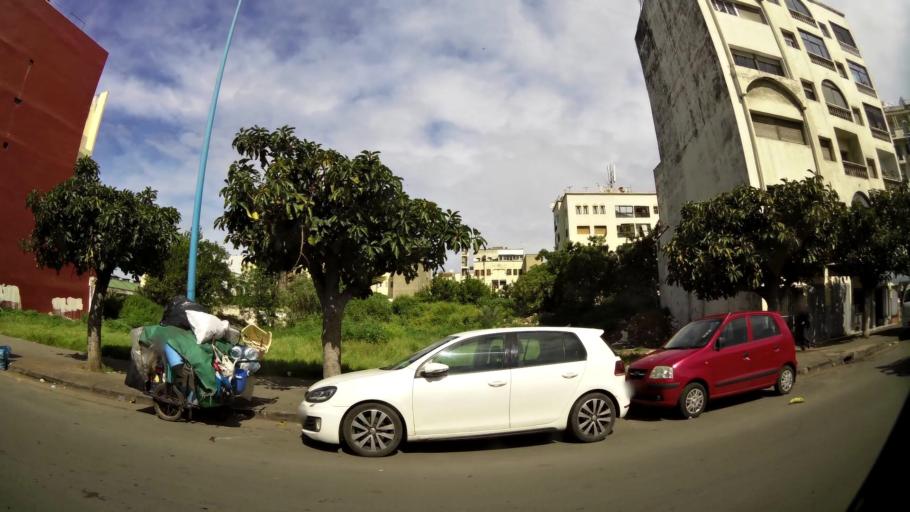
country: MA
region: Grand Casablanca
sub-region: Casablanca
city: Casablanca
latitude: 33.5830
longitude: -7.5820
